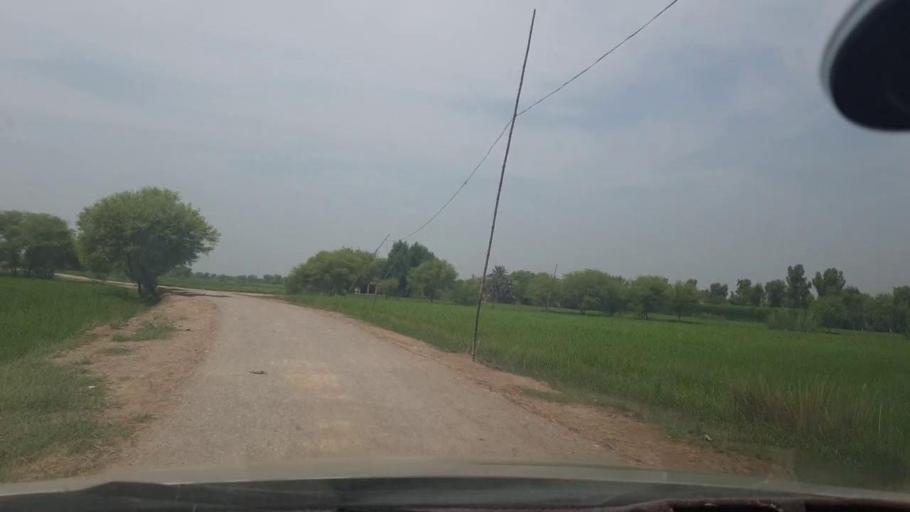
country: PK
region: Sindh
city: Jacobabad
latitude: 28.2422
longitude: 68.4306
